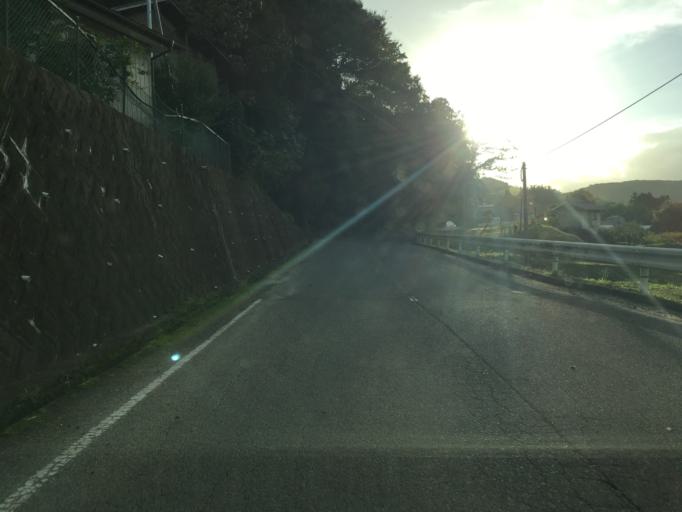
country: JP
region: Fukushima
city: Yanagawamachi-saiwaicho
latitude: 37.8999
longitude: 140.6607
